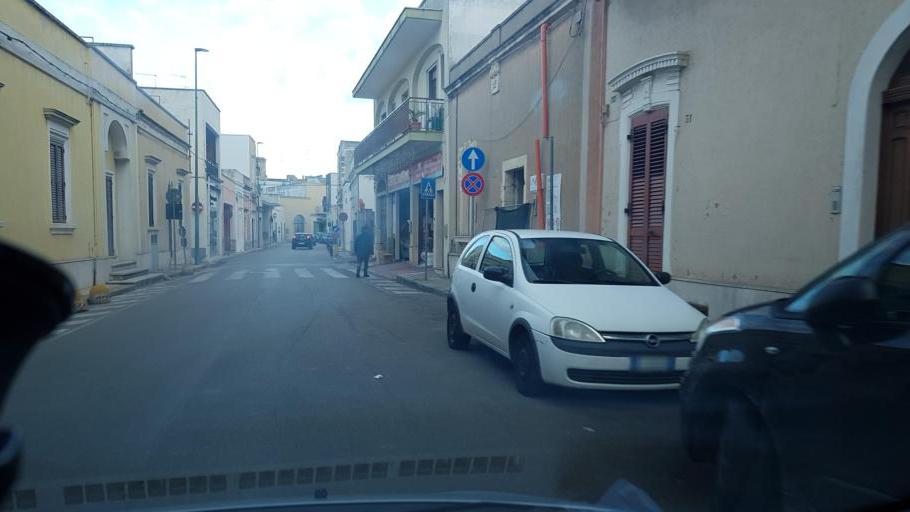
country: IT
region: Apulia
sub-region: Provincia di Lecce
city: Veglie
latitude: 40.3352
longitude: 17.9677
